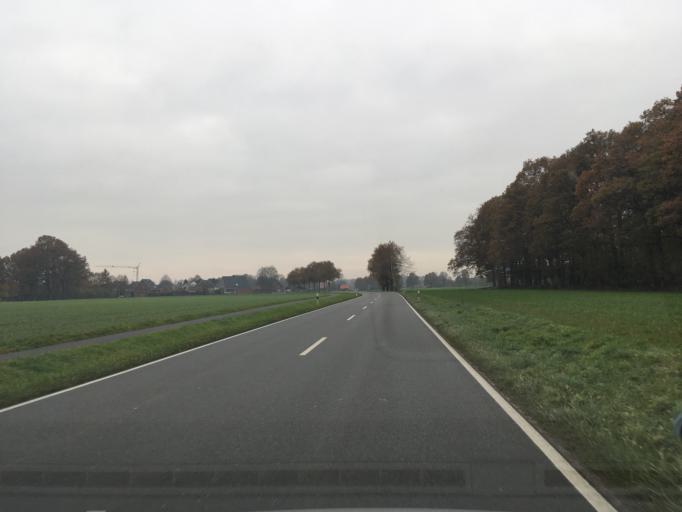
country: DE
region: North Rhine-Westphalia
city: Stadtlohn
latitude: 51.9858
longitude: 6.9560
